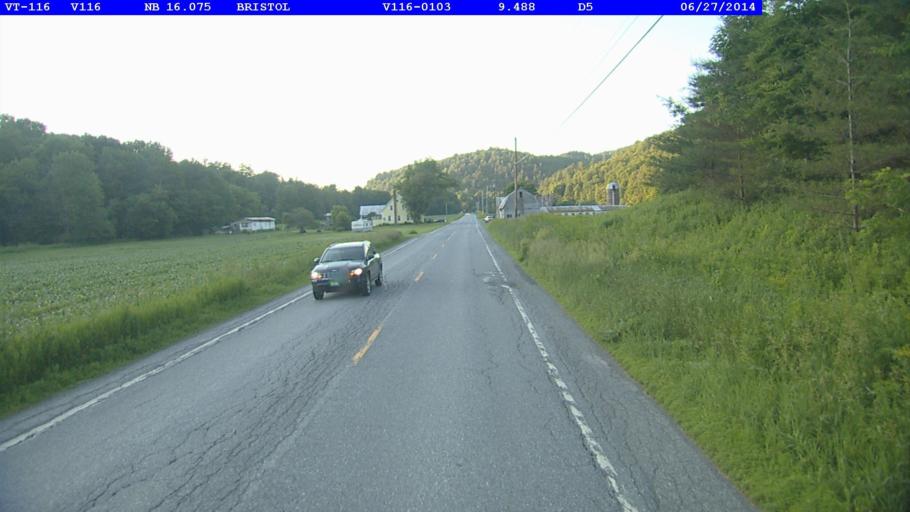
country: US
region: Vermont
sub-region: Addison County
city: Bristol
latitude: 44.1474
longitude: -73.0455
